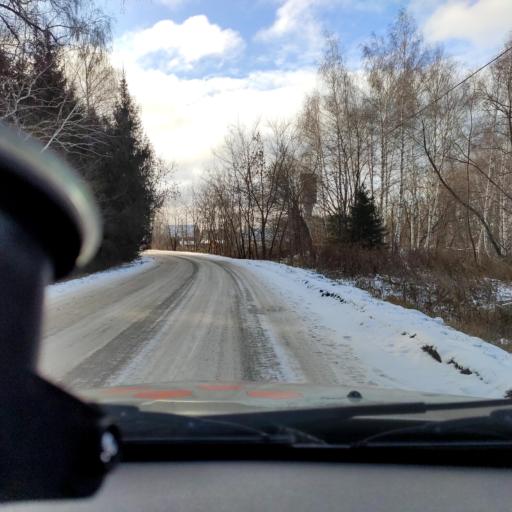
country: RU
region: Bashkortostan
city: Avdon
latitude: 54.7802
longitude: 55.7559
